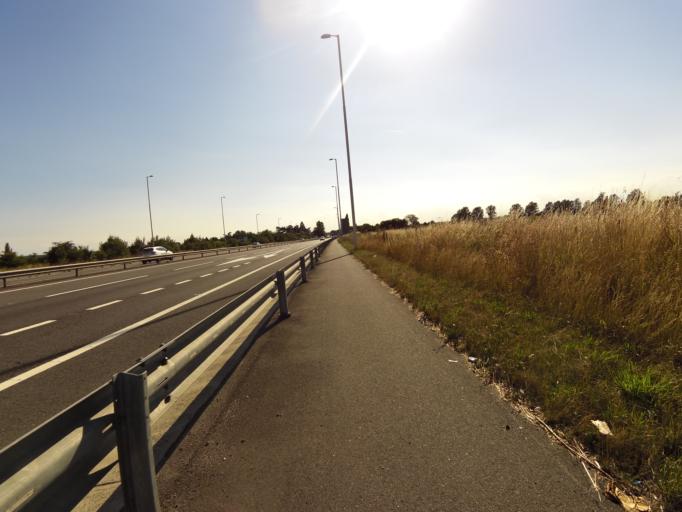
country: GB
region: England
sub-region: Essex
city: Kelvedon
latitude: 51.8246
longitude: 0.6823
